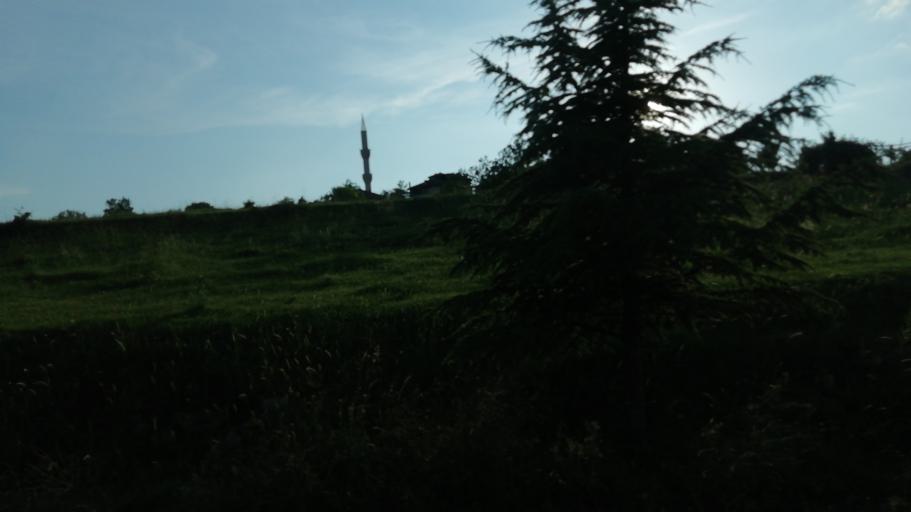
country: TR
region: Karabuk
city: Karabuk
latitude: 41.1275
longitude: 32.6217
